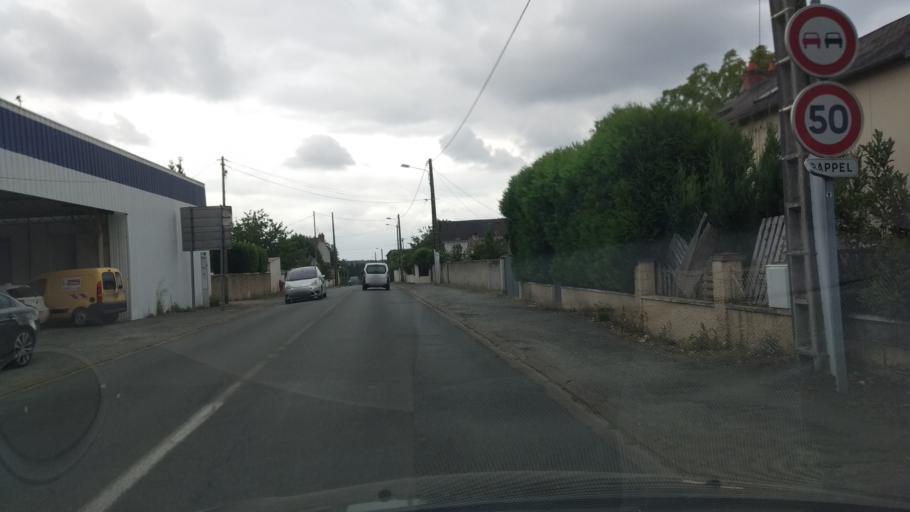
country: FR
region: Poitou-Charentes
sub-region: Departement de la Vienne
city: Saint-Benoit
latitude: 46.5630
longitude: 0.3562
